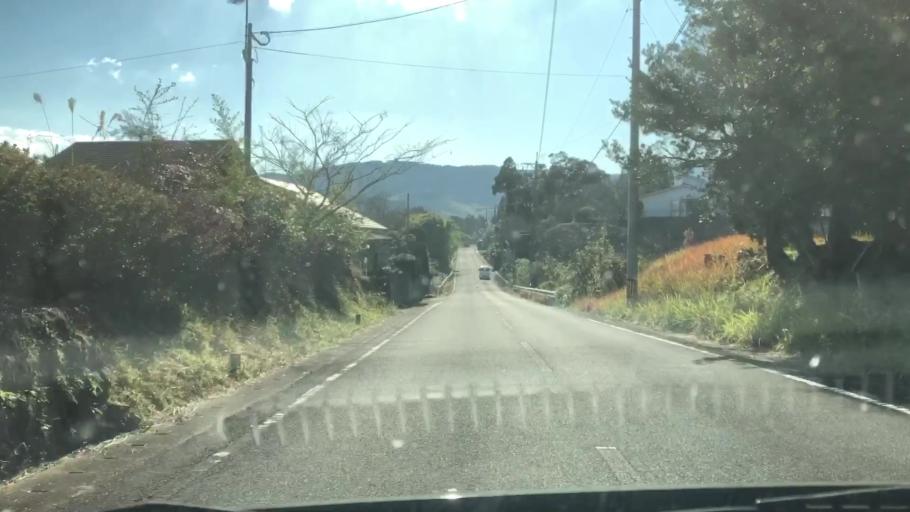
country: JP
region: Kagoshima
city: Satsumasendai
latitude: 31.8577
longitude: 130.3648
